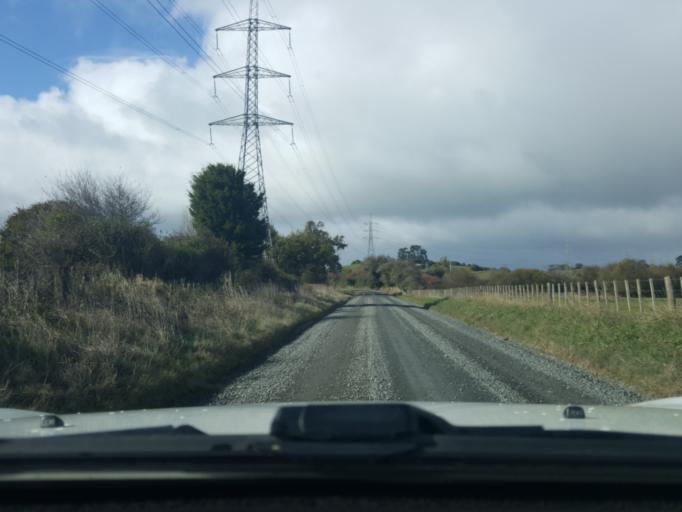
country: NZ
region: Waikato
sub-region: Waikato District
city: Te Kauwhata
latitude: -37.4199
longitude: 175.0705
